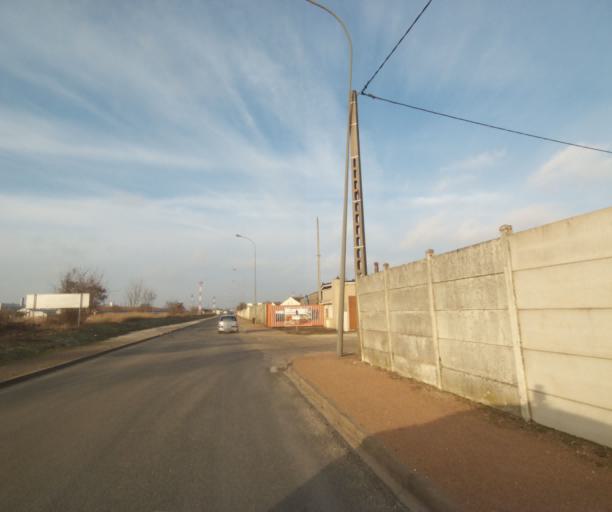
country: FR
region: Champagne-Ardenne
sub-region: Departement de la Haute-Marne
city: Saint-Dizier
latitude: 48.6454
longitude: 4.9435
